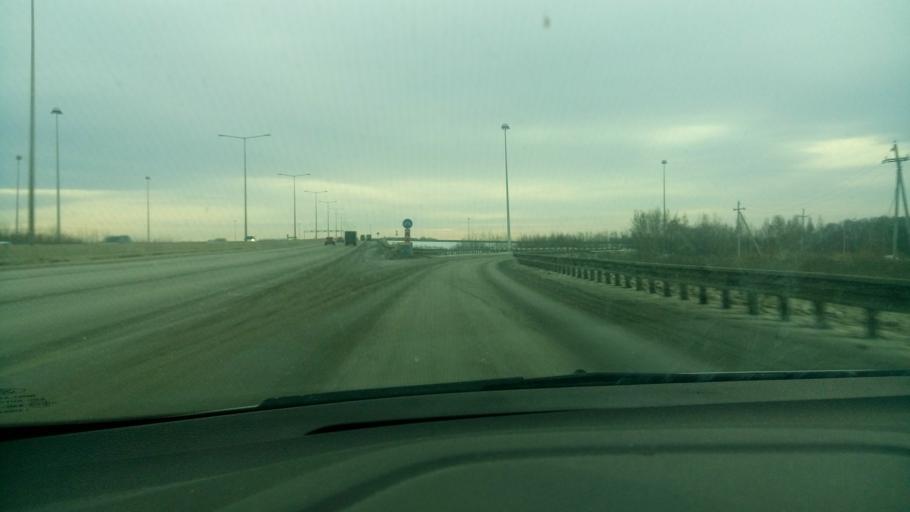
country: RU
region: Sverdlovsk
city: Istok
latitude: 56.7621
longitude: 60.7609
